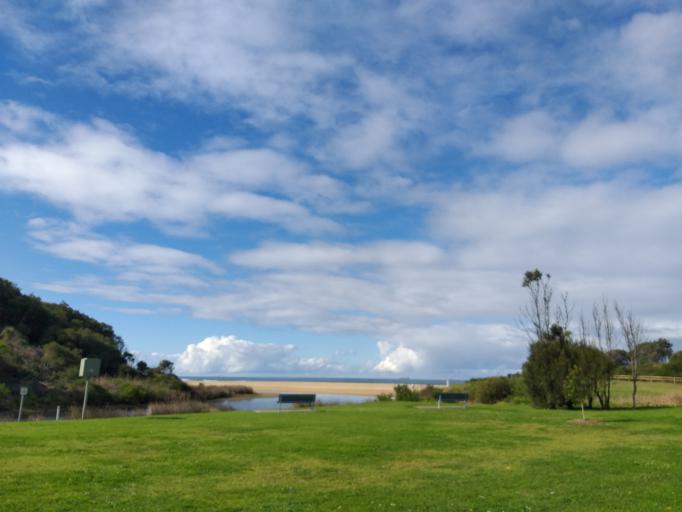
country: AU
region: New South Wales
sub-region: Wollongong
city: East Corrimal
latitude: -34.3761
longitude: 150.9193
